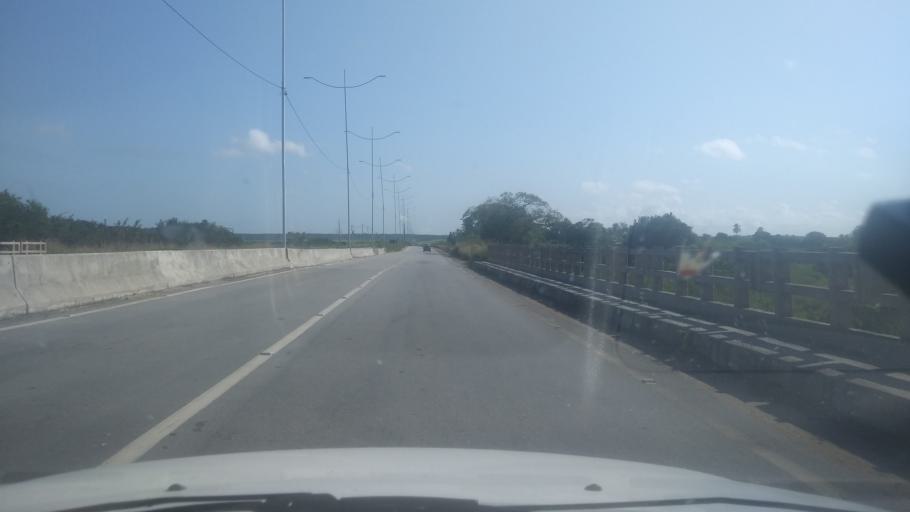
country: BR
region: Rio Grande do Norte
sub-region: Sao Goncalo Do Amarante
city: Sao Goncalo do Amarante
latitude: -5.8100
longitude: -35.3607
